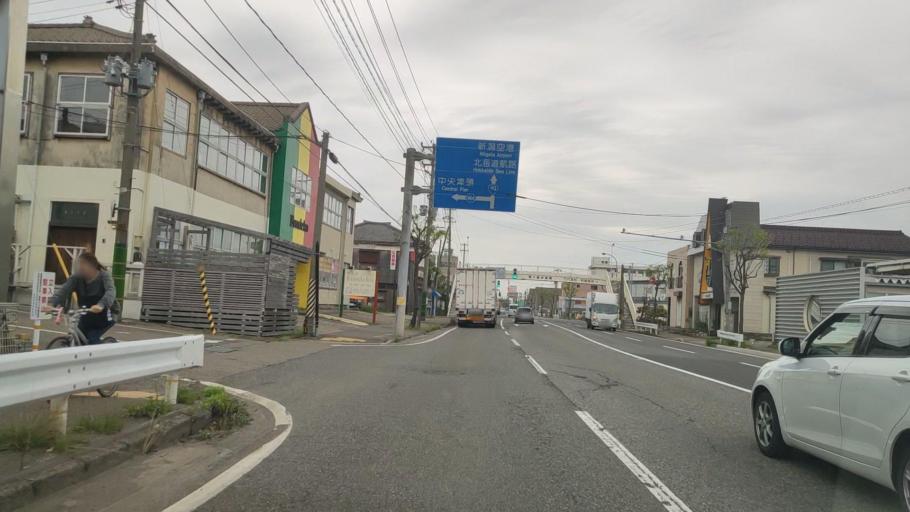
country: JP
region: Niigata
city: Niigata-shi
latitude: 37.9278
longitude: 139.0668
